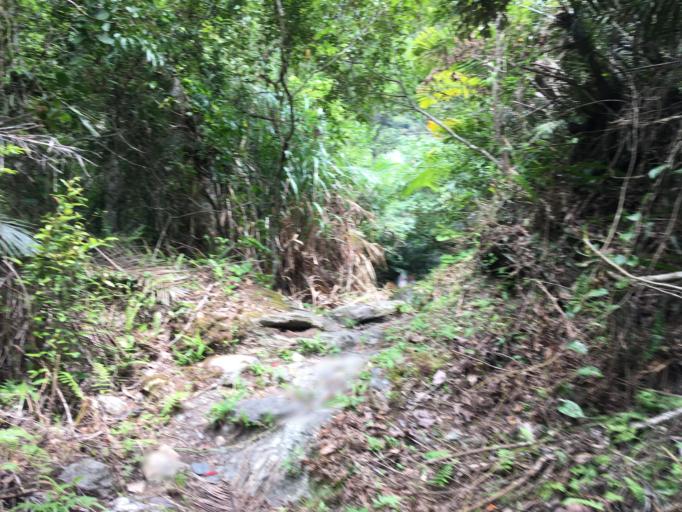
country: TW
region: Taiwan
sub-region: Yilan
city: Yilan
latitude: 24.4293
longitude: 121.6918
